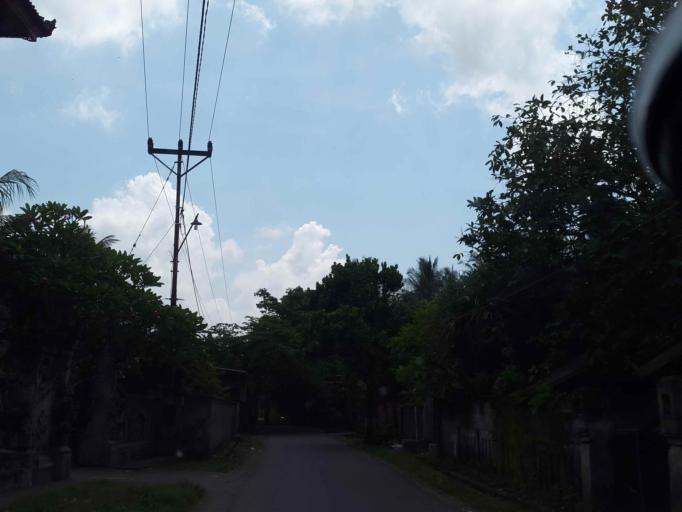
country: ID
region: West Nusa Tenggara
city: Mambalan
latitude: -8.5434
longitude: 116.1075
